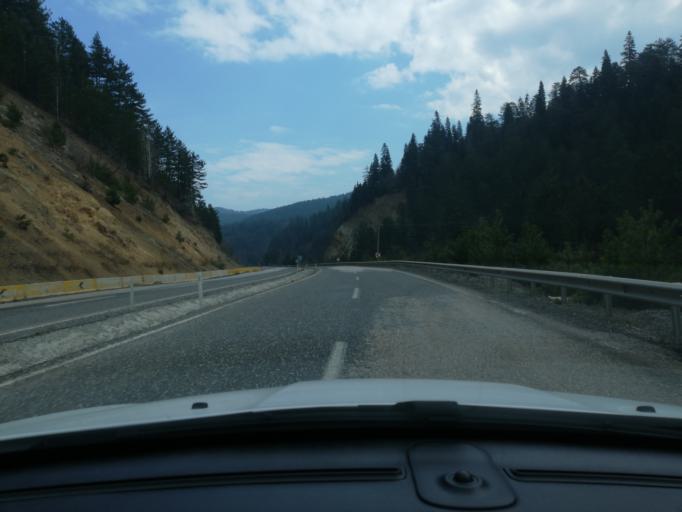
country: TR
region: Kastamonu
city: Kuzyaka
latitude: 41.1527
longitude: 33.7870
